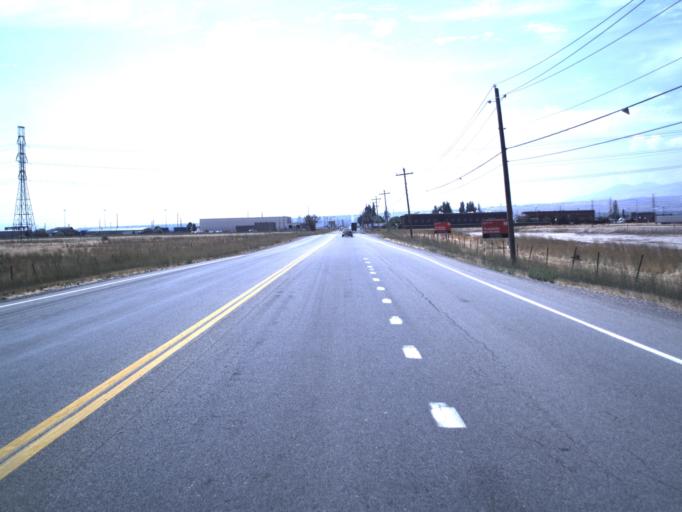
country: US
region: Utah
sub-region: Salt Lake County
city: West Valley City
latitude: 40.7608
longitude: -112.0250
